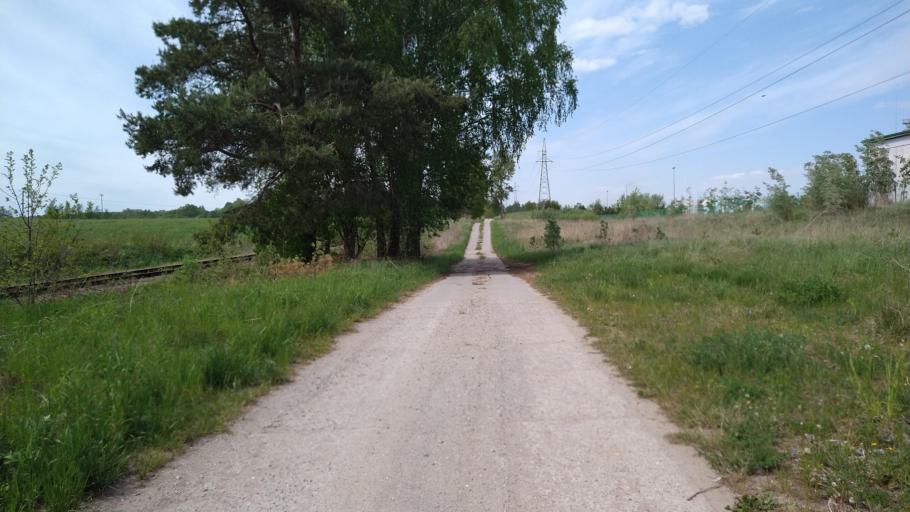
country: PL
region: Warmian-Masurian Voivodeship
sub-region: Powiat olsztynski
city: Olsztyn
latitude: 53.7875
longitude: 20.5502
